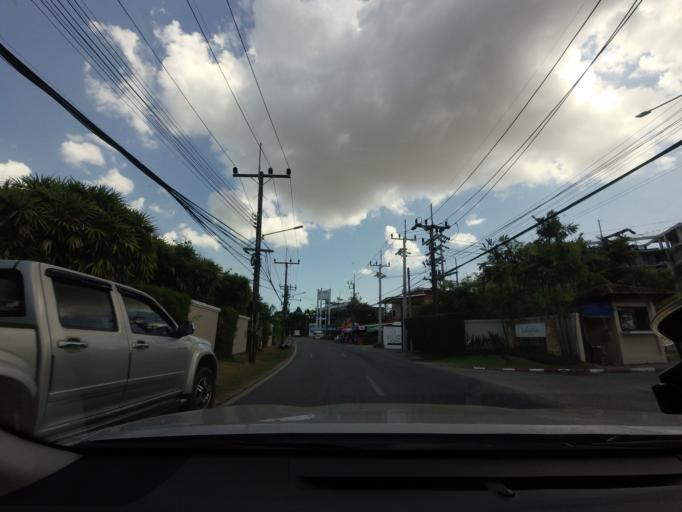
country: TH
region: Phuket
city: Thalang
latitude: 8.0183
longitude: 98.3049
